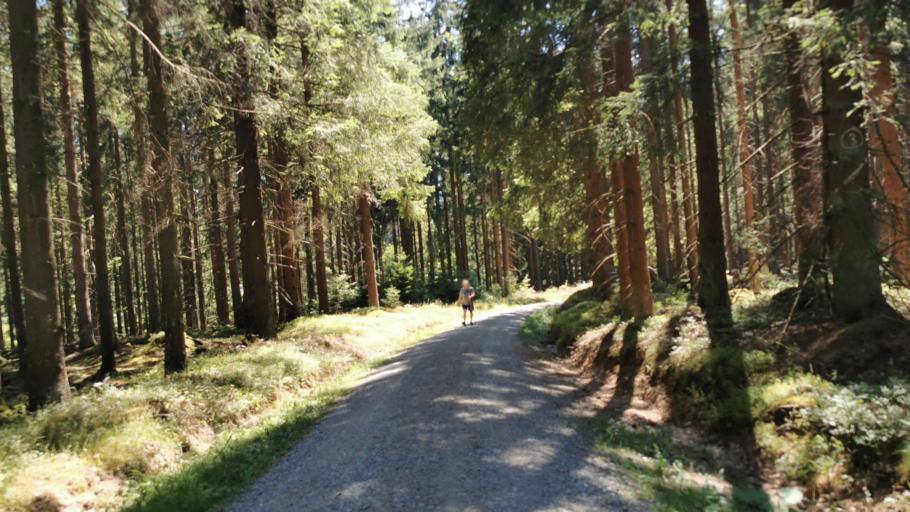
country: DE
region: Bavaria
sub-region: Upper Franconia
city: Pressig
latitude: 50.4099
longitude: 11.2923
